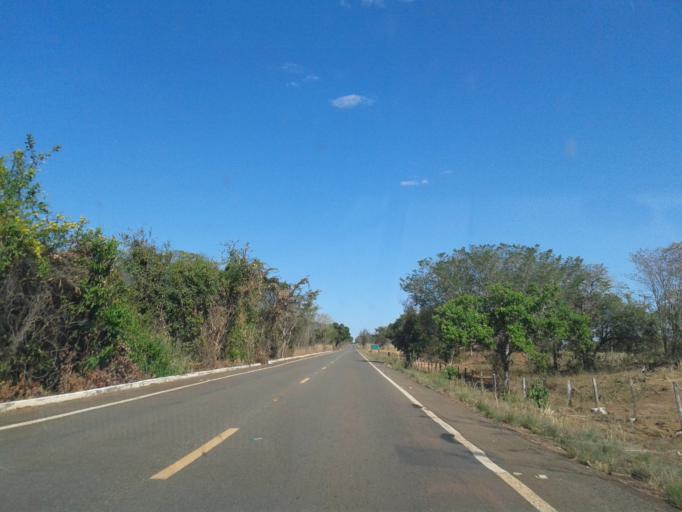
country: BR
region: Goias
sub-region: Sao Miguel Do Araguaia
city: Sao Miguel do Araguaia
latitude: -13.9108
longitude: -50.3247
